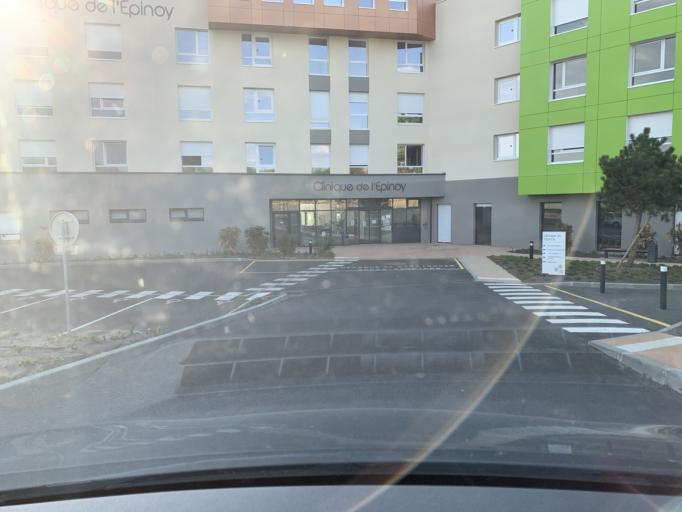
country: FR
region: Nord-Pas-de-Calais
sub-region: Departement du Nord
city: Cambrai
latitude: 50.1628
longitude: 3.2236
